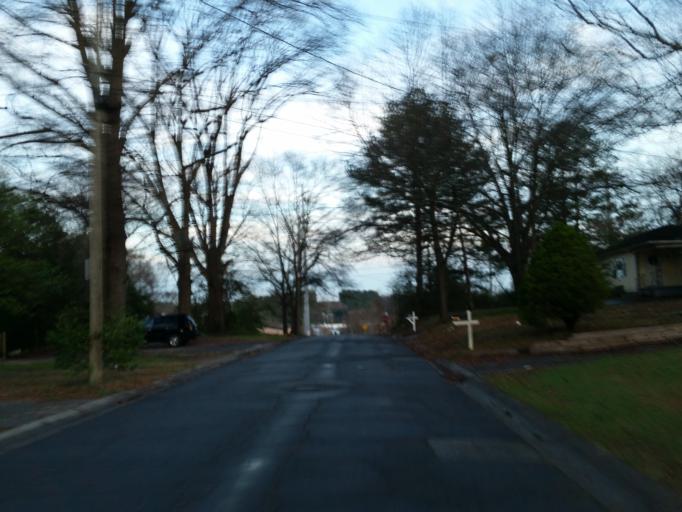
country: US
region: Georgia
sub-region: Cobb County
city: Marietta
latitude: 33.9629
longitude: -84.5383
